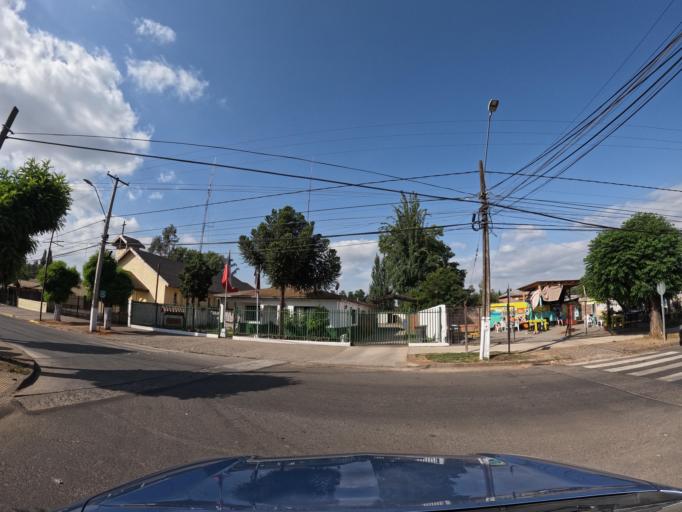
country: CL
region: Maule
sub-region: Provincia de Curico
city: Molina
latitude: -35.2819
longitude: -71.2578
